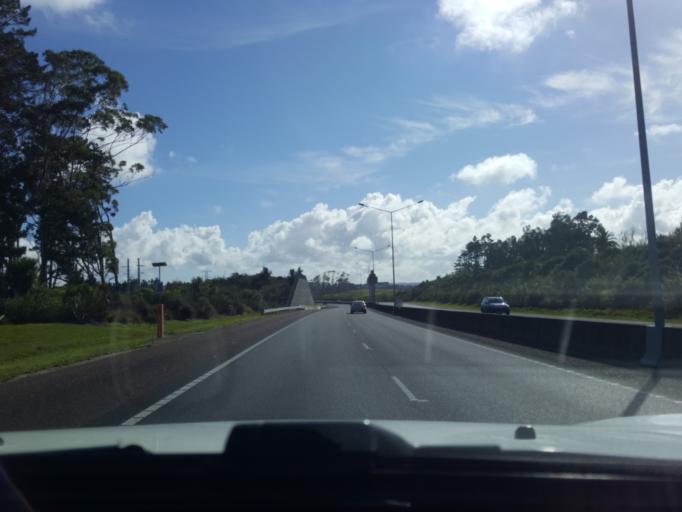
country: NZ
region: Auckland
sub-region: Auckland
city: Rosebank
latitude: -36.8104
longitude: 174.6097
